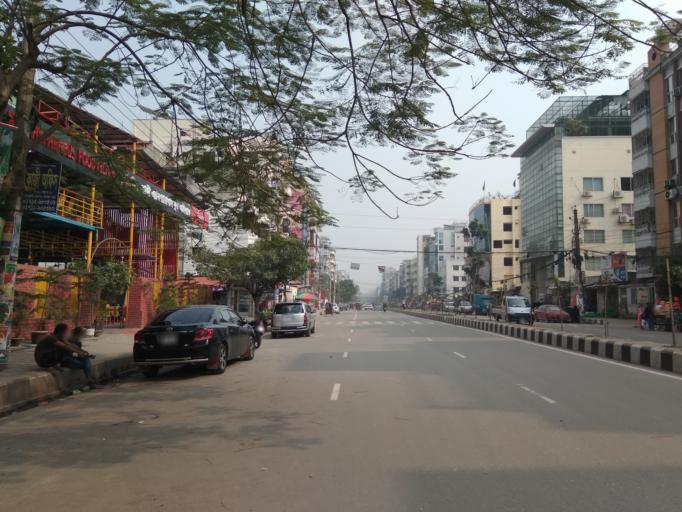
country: BD
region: Dhaka
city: Tungi
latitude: 23.8694
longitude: 90.3843
